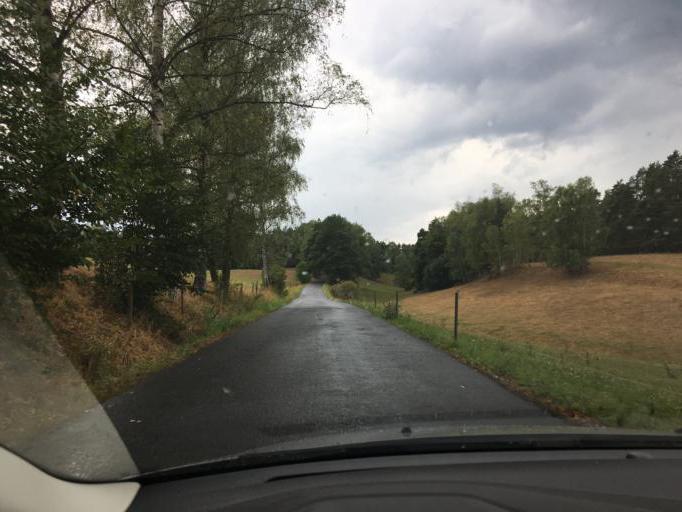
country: CZ
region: Ustecky
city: Ceska Kamenice
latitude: 50.8152
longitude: 14.3448
